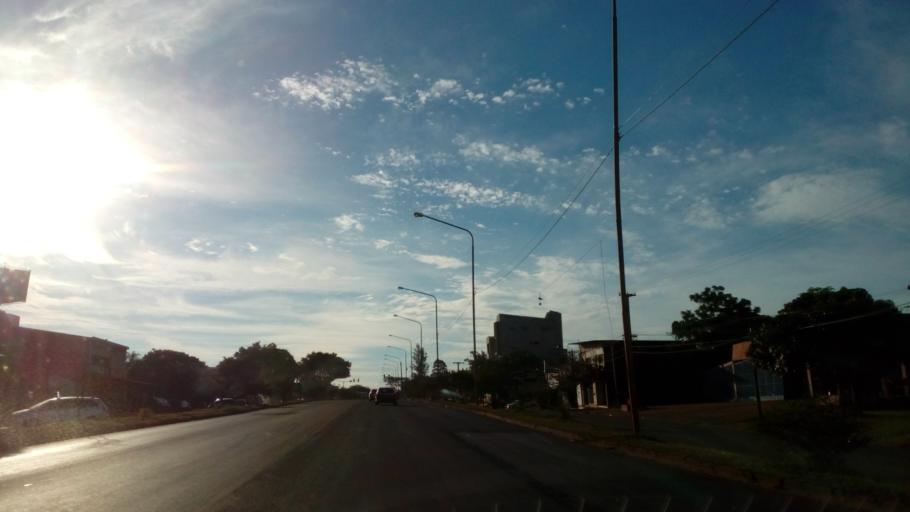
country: AR
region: Misiones
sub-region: Departamento de Capital
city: Posadas
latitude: -27.4043
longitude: -55.9045
